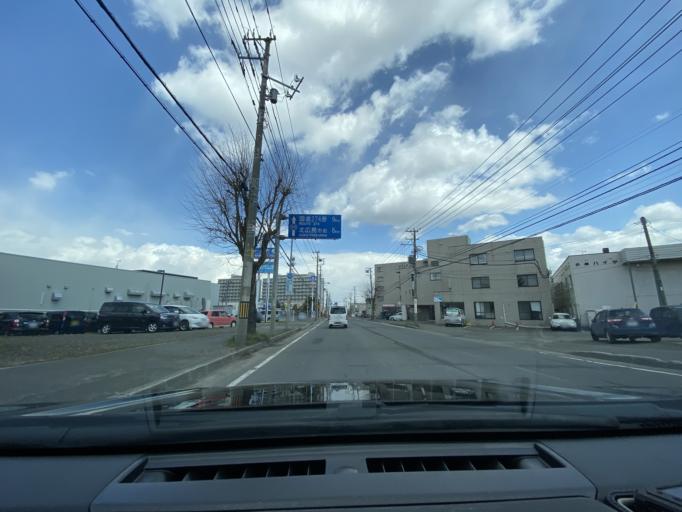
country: JP
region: Hokkaido
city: Kitahiroshima
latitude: 42.9735
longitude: 141.4782
